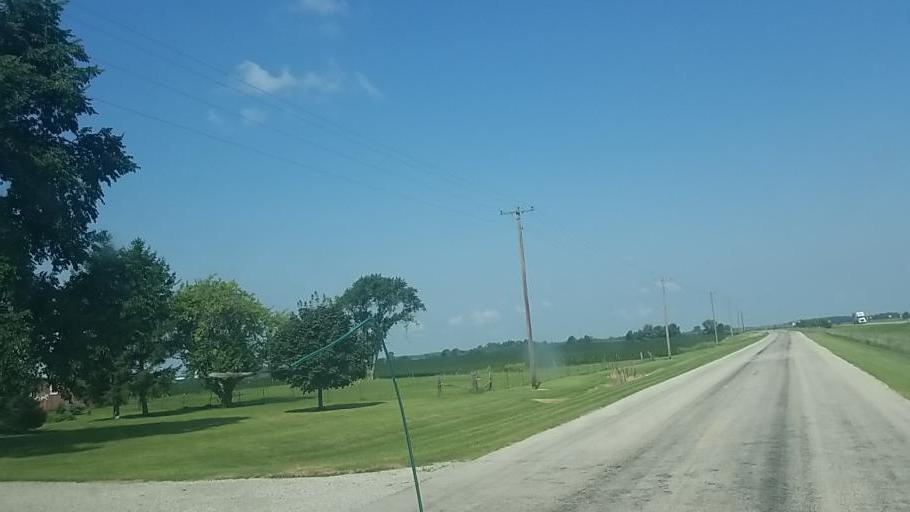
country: US
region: Ohio
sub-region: Marion County
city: Marion
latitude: 40.7133
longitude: -83.1744
